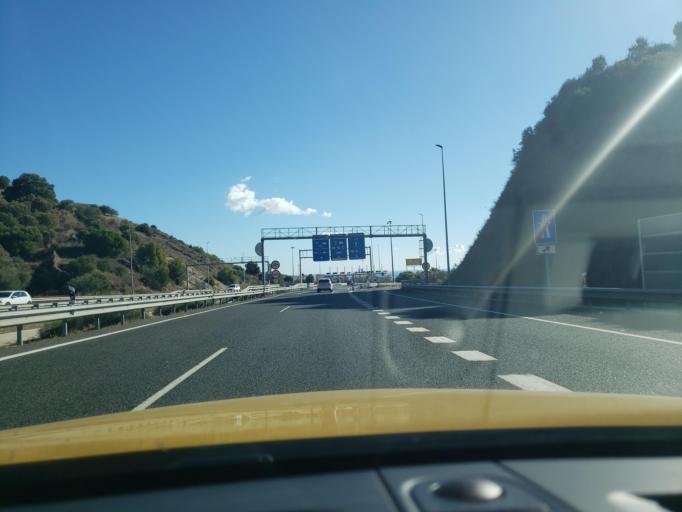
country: ES
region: Andalusia
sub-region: Provincia de Malaga
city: Fuengirola
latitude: 36.5065
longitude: -4.7215
